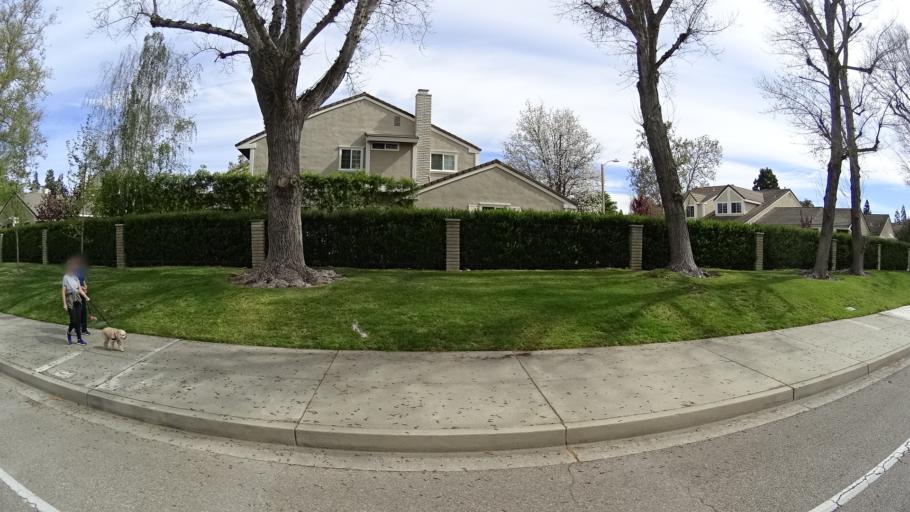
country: US
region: California
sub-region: Los Angeles County
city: Westlake Village
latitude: 34.1488
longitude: -118.8213
